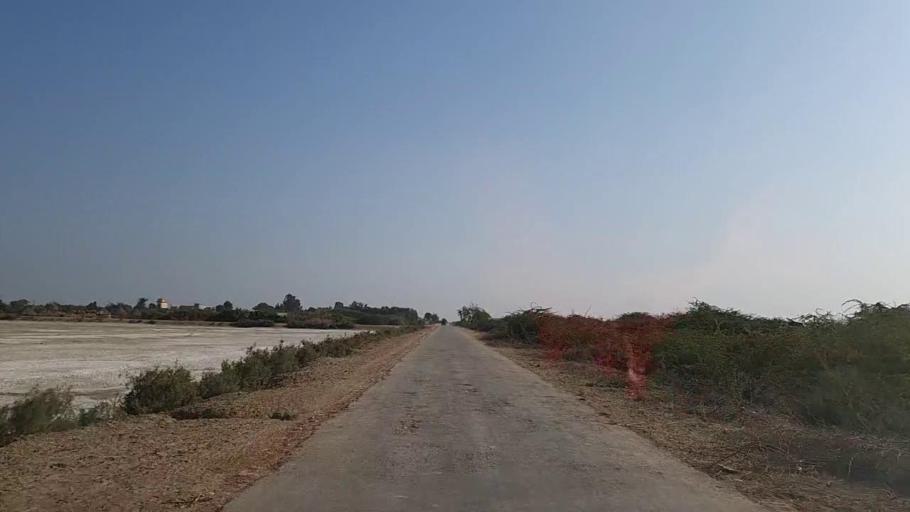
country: PK
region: Sindh
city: Tando Mittha Khan
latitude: 25.9305
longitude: 69.0628
